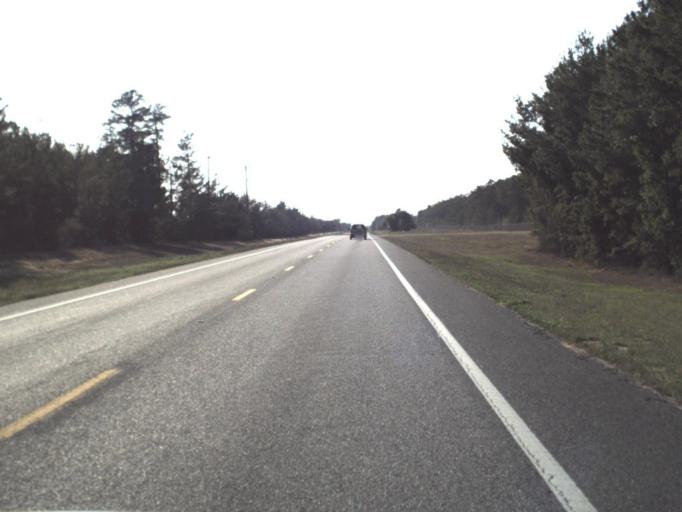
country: US
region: Florida
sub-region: Bay County
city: Lynn Haven
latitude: 30.4259
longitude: -85.6293
